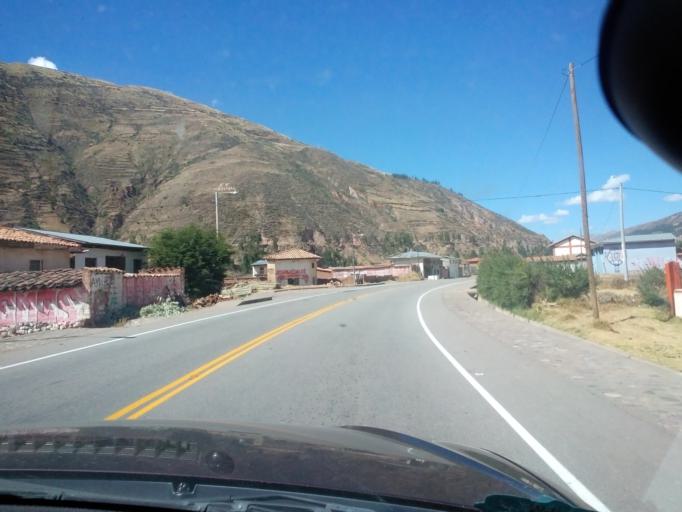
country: PE
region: Cusco
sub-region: Provincia de Canchis
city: Checacupe
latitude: -13.9941
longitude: -71.4621
